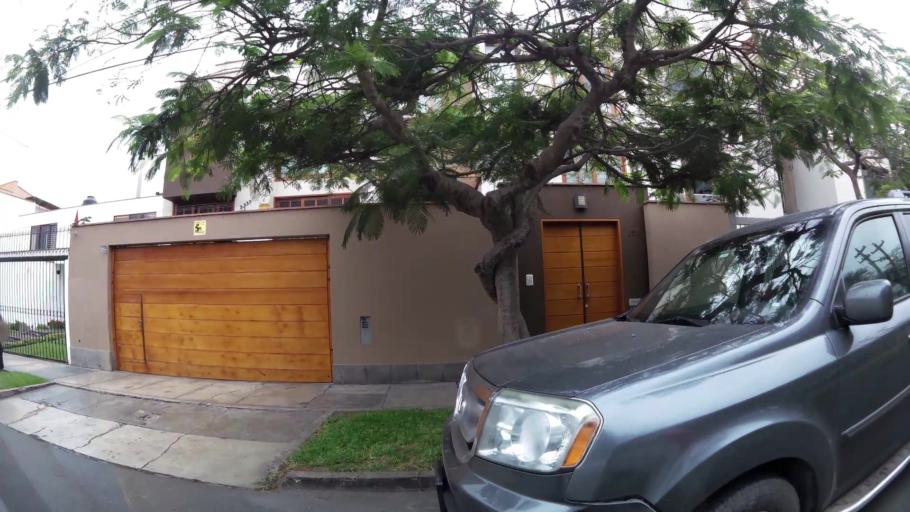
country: PE
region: Lima
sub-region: Lima
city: Surco
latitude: -12.1226
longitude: -77.0098
